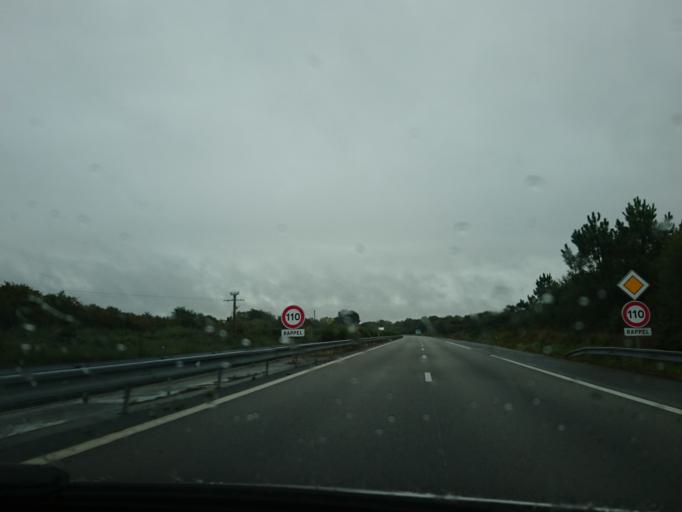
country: FR
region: Brittany
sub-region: Departement du Morbihan
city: Surzur
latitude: 47.6080
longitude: -2.6077
